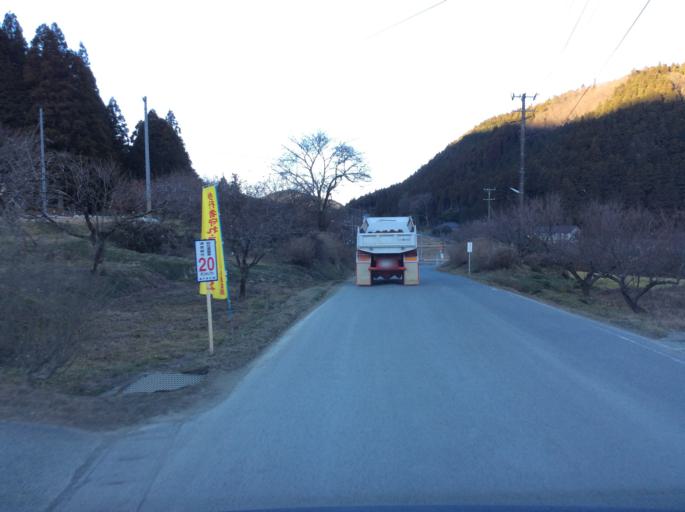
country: JP
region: Ibaraki
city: Kitaibaraki
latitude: 36.8834
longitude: 140.7218
